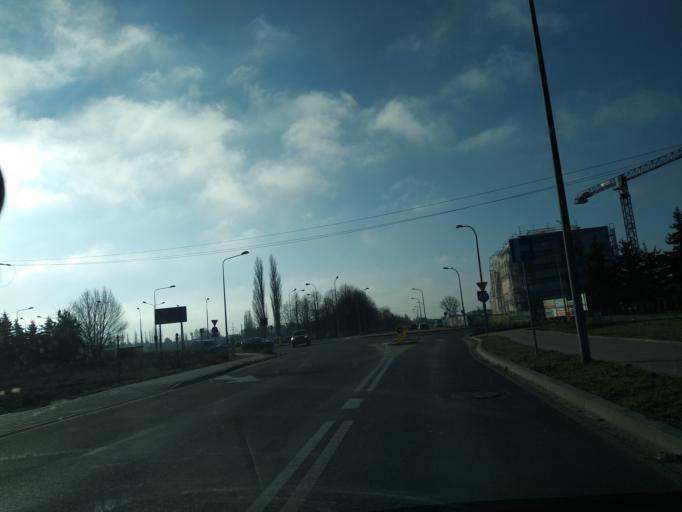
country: PL
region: Masovian Voivodeship
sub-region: Powiat piaseczynski
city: Piaseczno
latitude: 52.0886
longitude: 21.0132
